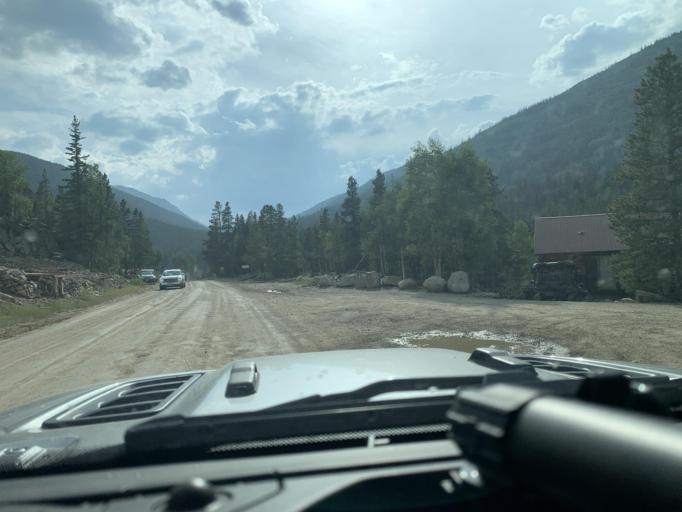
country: US
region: Colorado
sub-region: Chaffee County
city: Buena Vista
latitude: 38.7056
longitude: -106.3420
